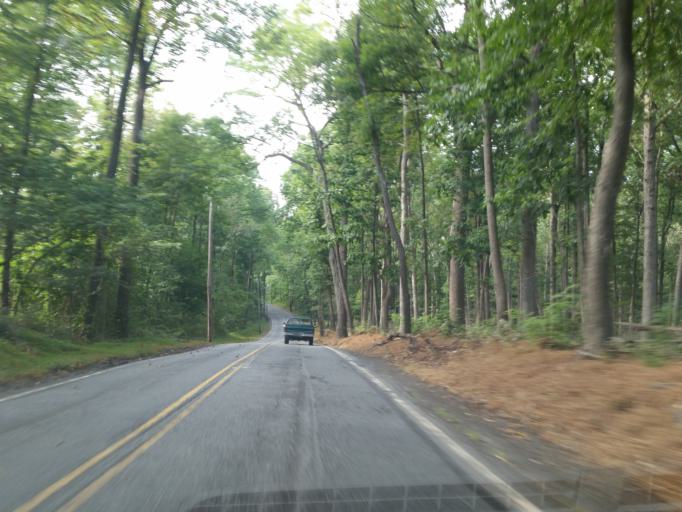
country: US
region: Pennsylvania
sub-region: Lebanon County
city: Campbelltown
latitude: 40.2317
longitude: -76.5055
